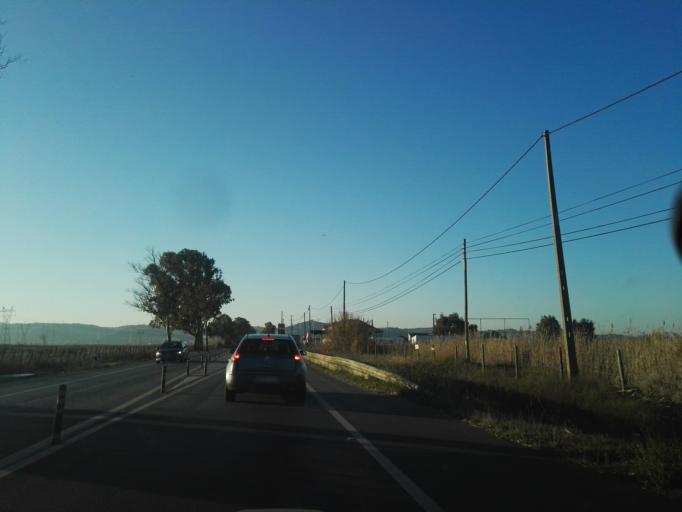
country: PT
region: Lisbon
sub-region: Vila Franca de Xira
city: Vila Franca de Xira
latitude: 38.9418
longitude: -8.9441
